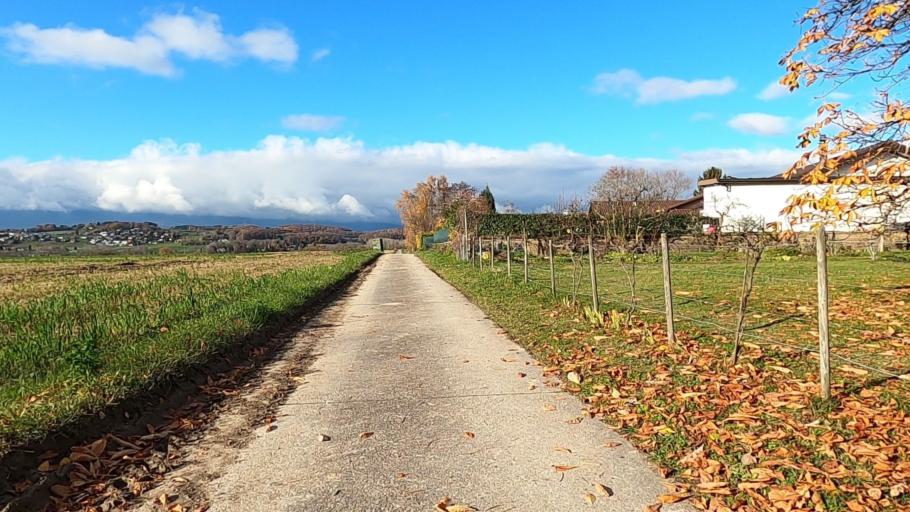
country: CH
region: Vaud
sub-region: Morges District
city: Saint-Prex
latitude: 46.5149
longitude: 6.4482
